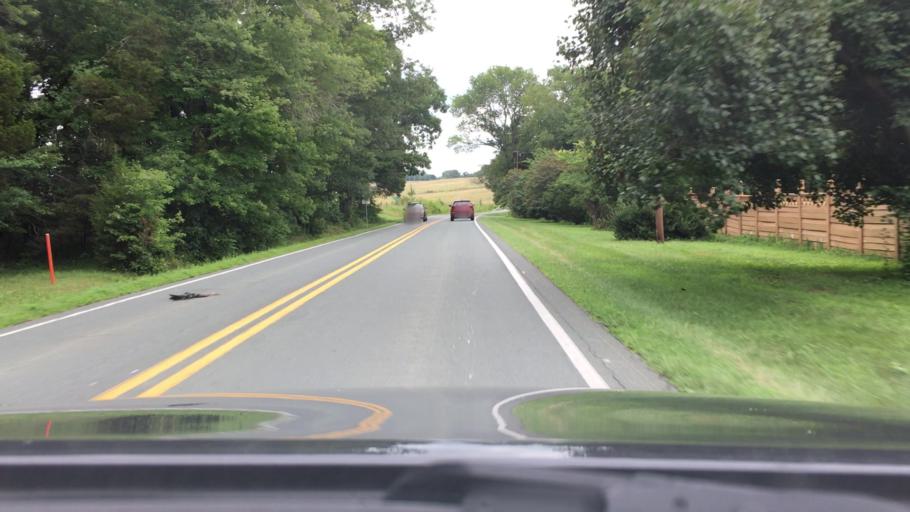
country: US
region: Virginia
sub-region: Orange County
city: Gordonsville
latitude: 38.0924
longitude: -78.2683
